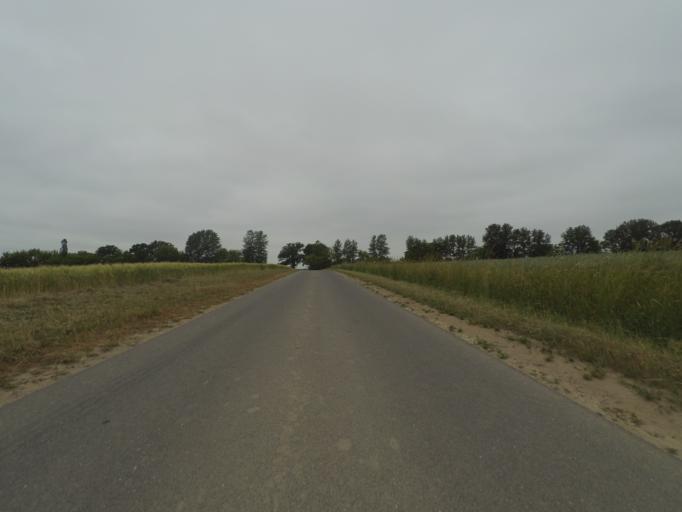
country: DE
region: Mecklenburg-Vorpommern
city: Goldberg
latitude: 53.5546
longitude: 12.0295
